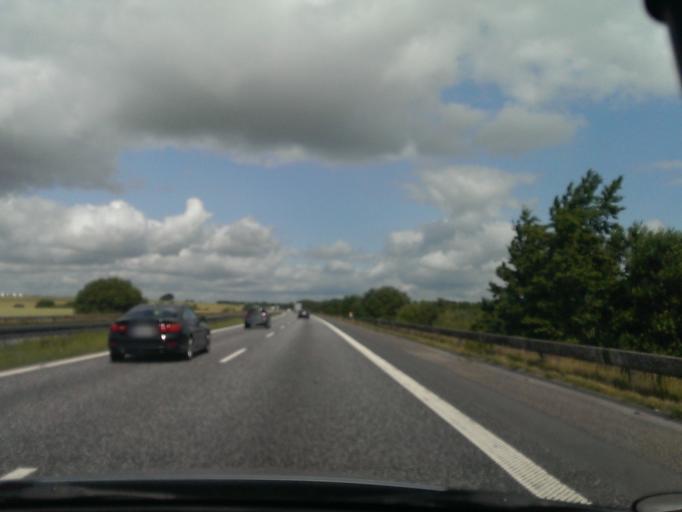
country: DK
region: Central Jutland
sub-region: Randers Kommune
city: Spentrup
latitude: 56.5162
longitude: 9.9629
